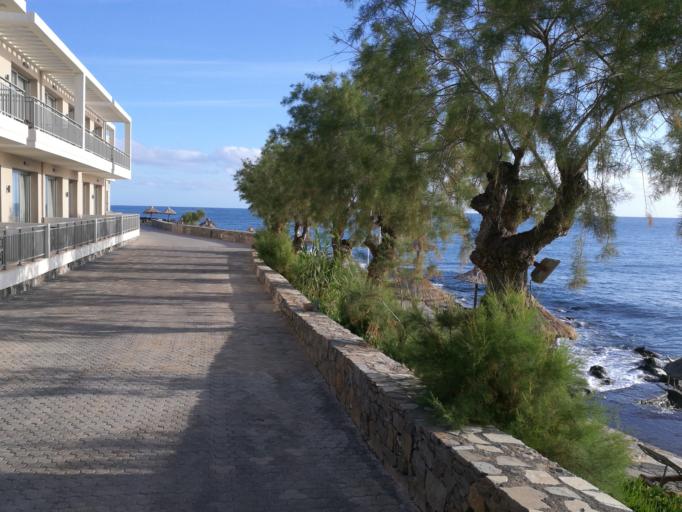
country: GR
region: Crete
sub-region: Nomos Irakleiou
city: Stalis
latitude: 35.3039
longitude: 25.4223
